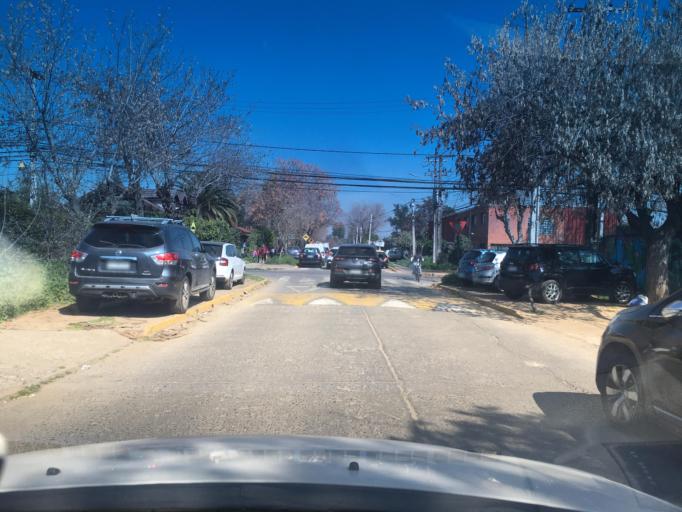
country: CL
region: Santiago Metropolitan
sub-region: Provincia de Santiago
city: Villa Presidente Frei, Nunoa, Santiago, Chile
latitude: -33.4656
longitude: -70.5711
